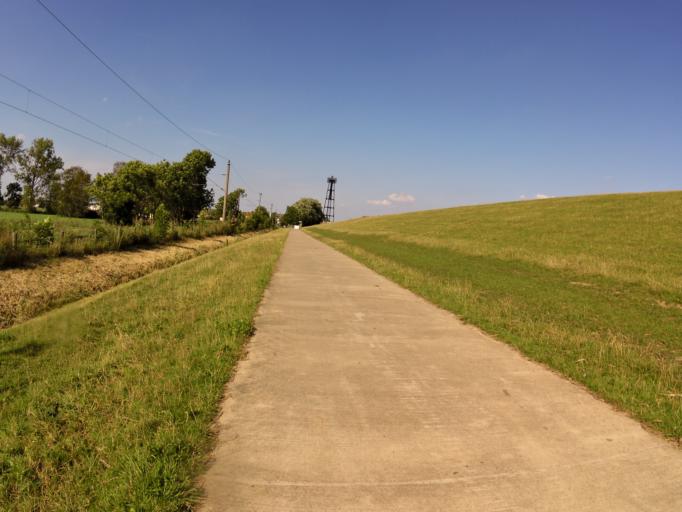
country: DE
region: Lower Saxony
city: Nordenham
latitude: 53.4633
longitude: 8.4754
